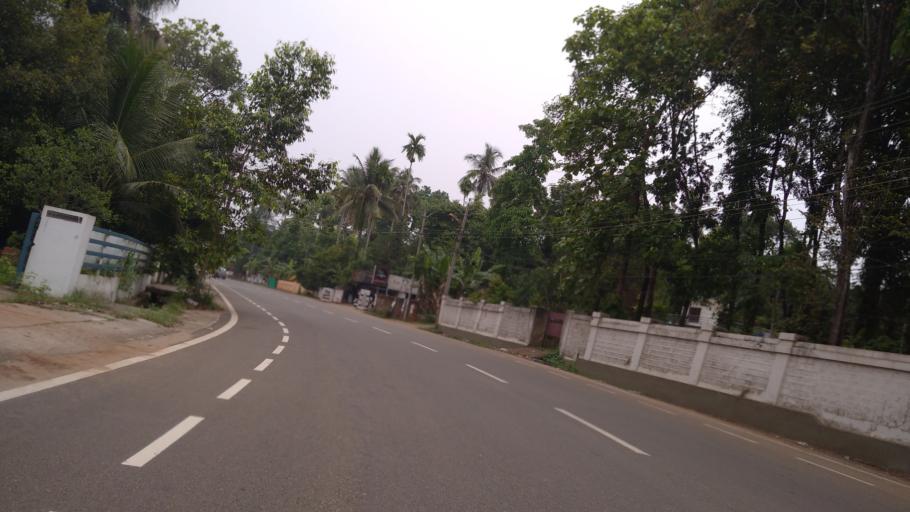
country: IN
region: Kerala
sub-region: Ernakulam
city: Angamali
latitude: 10.1838
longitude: 76.3970
